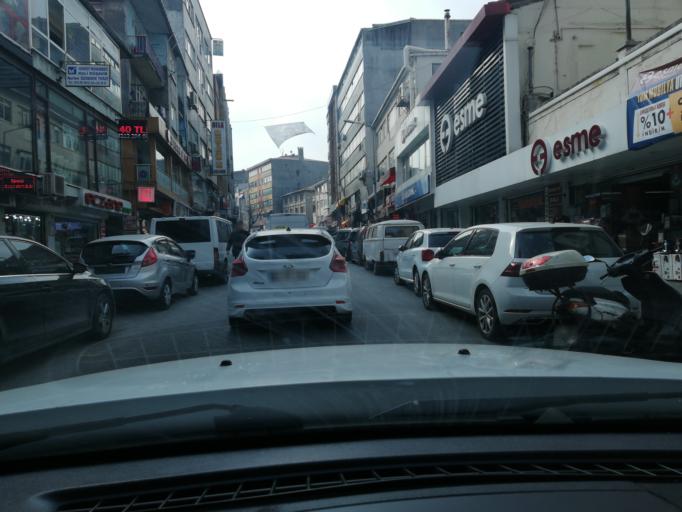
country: TR
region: Istanbul
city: Sisli
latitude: 41.0759
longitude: 28.9813
